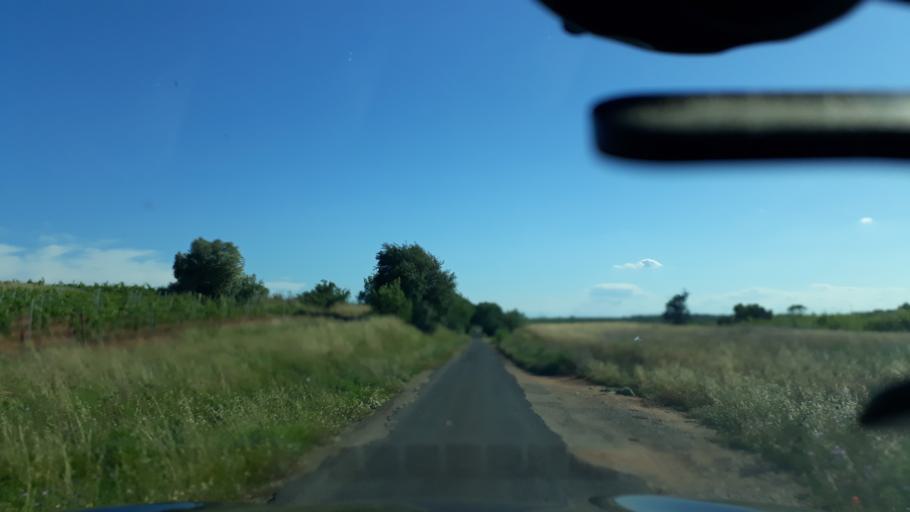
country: FR
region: Languedoc-Roussillon
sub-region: Departement de l'Herault
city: Marseillan
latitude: 43.3393
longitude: 3.5084
